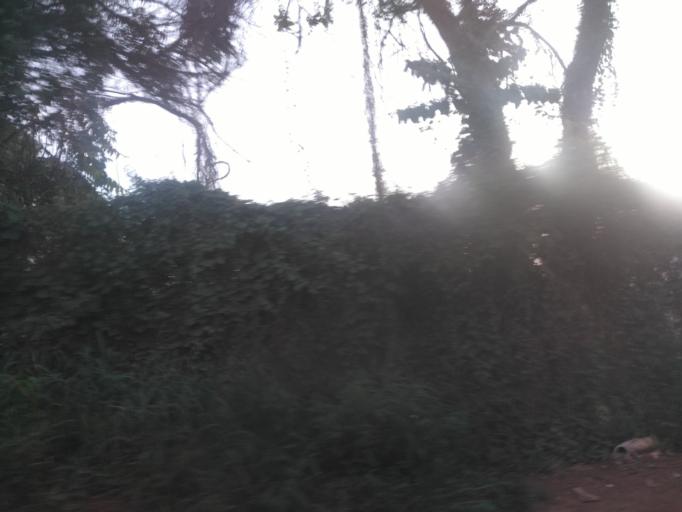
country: UG
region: Central Region
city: Kampala Central Division
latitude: 0.3404
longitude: 32.5787
